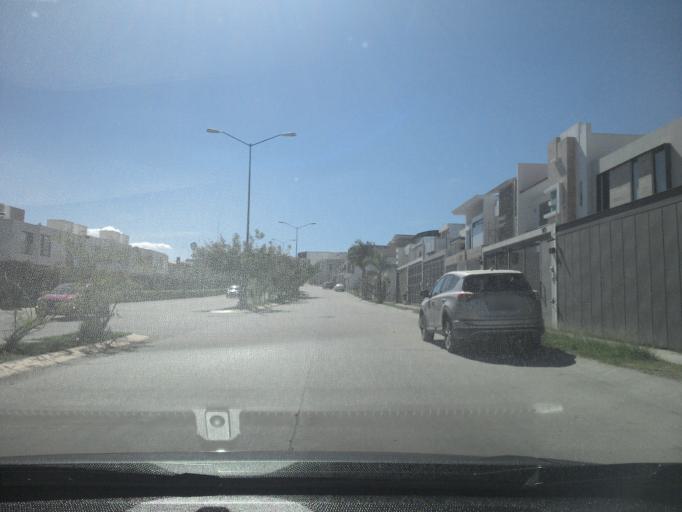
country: MX
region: Jalisco
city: Nuevo Mexico
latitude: 20.7532
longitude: -103.4122
